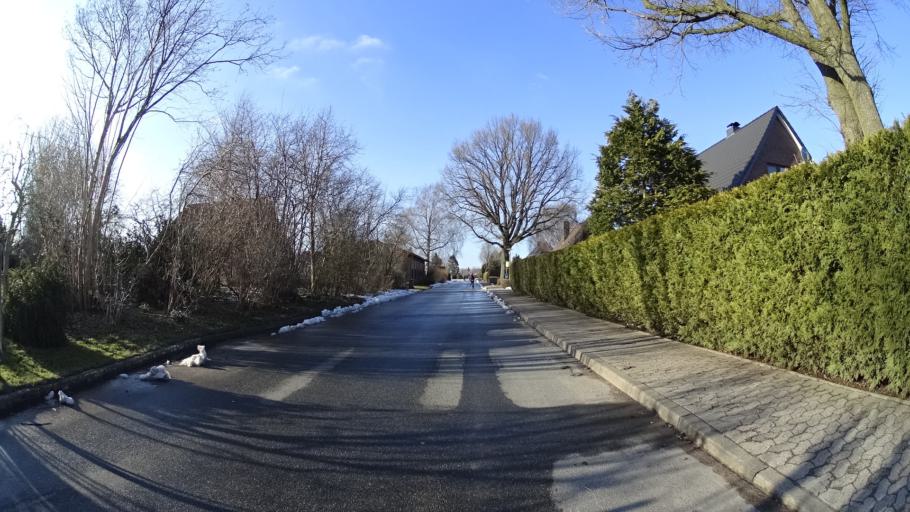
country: DE
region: Schleswig-Holstein
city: Martensrade
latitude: 54.2885
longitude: 10.3844
